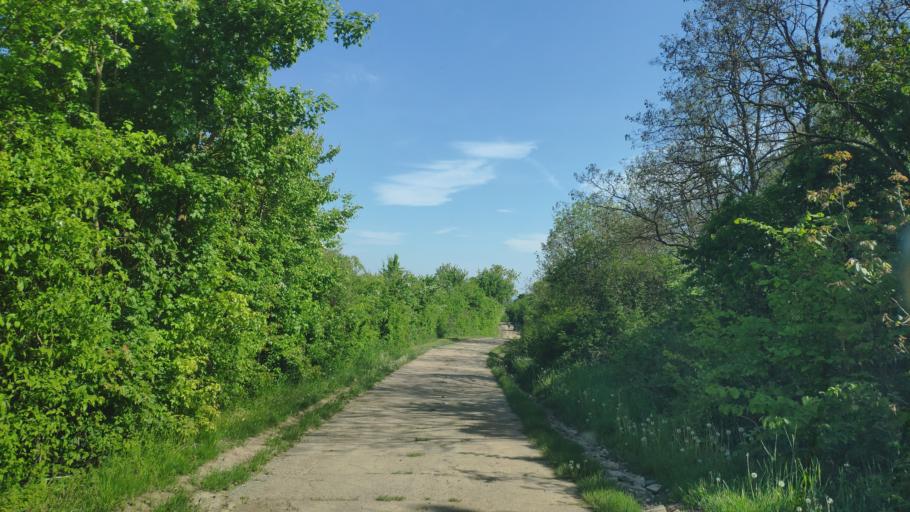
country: SK
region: Kosicky
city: Secovce
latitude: 48.6870
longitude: 21.6062
